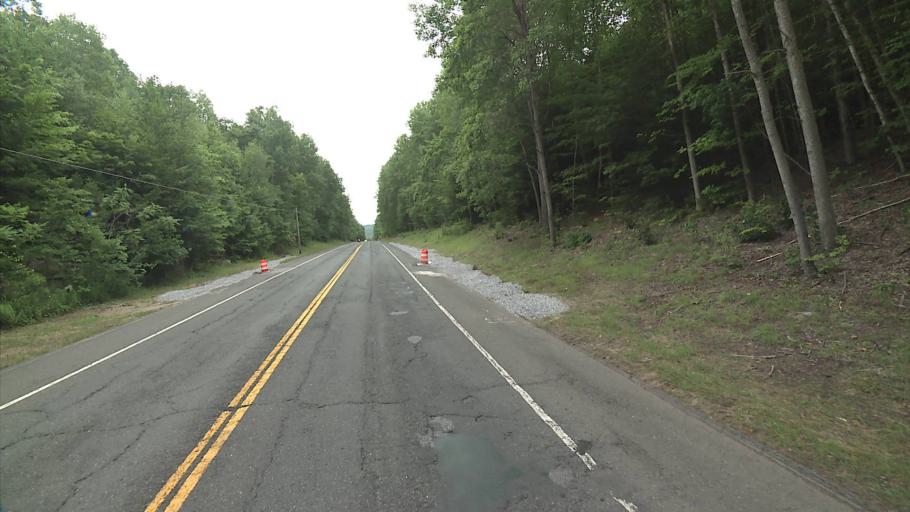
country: US
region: Connecticut
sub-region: Litchfield County
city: Winsted
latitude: 42.0321
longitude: -73.0559
